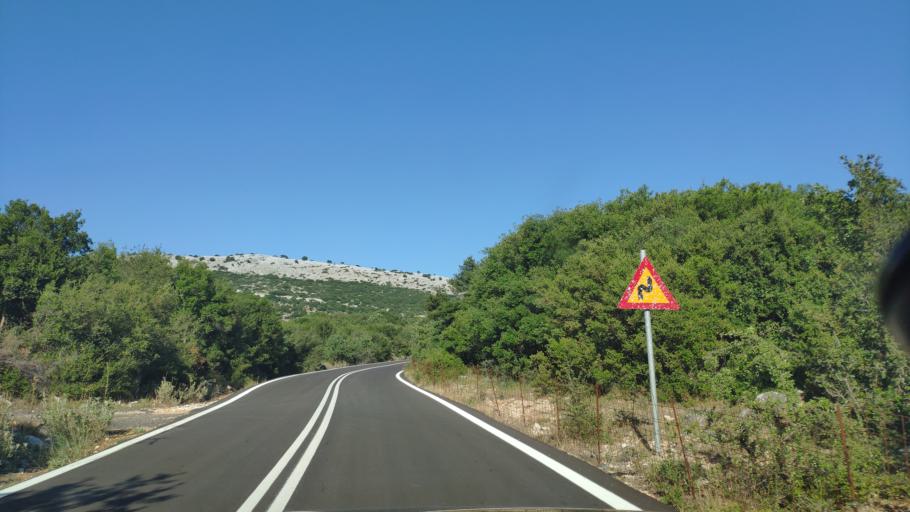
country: GR
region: West Greece
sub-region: Nomos Aitolias kai Akarnanias
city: Archontochorion
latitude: 38.6915
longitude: 21.0544
